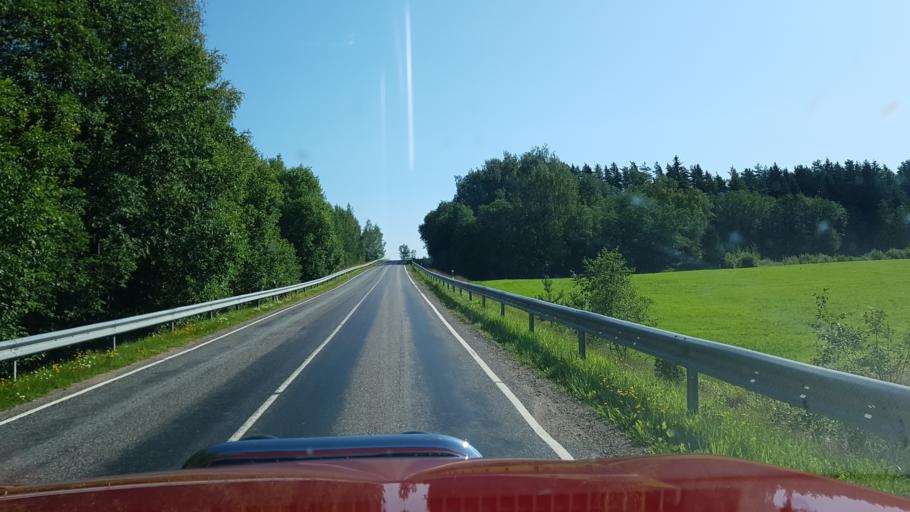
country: EE
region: Polvamaa
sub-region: Polva linn
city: Polva
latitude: 57.9854
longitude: 26.8839
